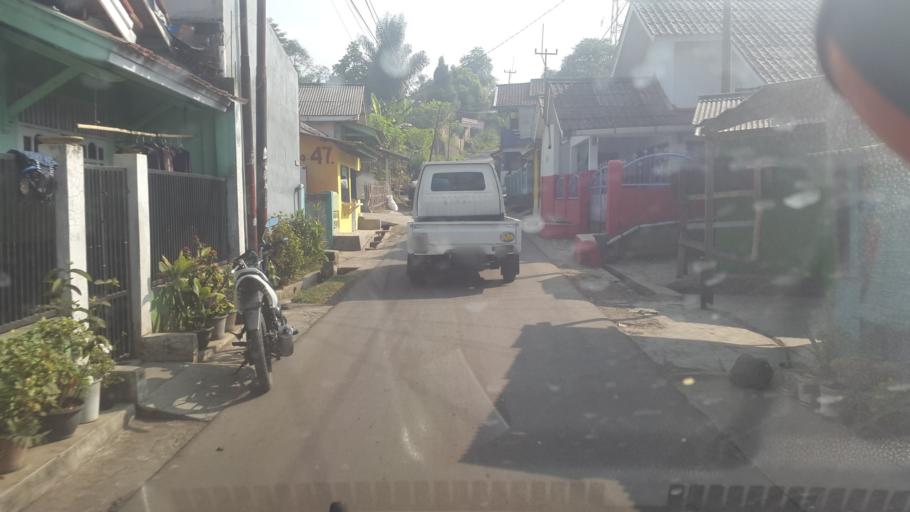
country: ID
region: West Java
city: Sukabumi
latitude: -6.9044
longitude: 106.9774
